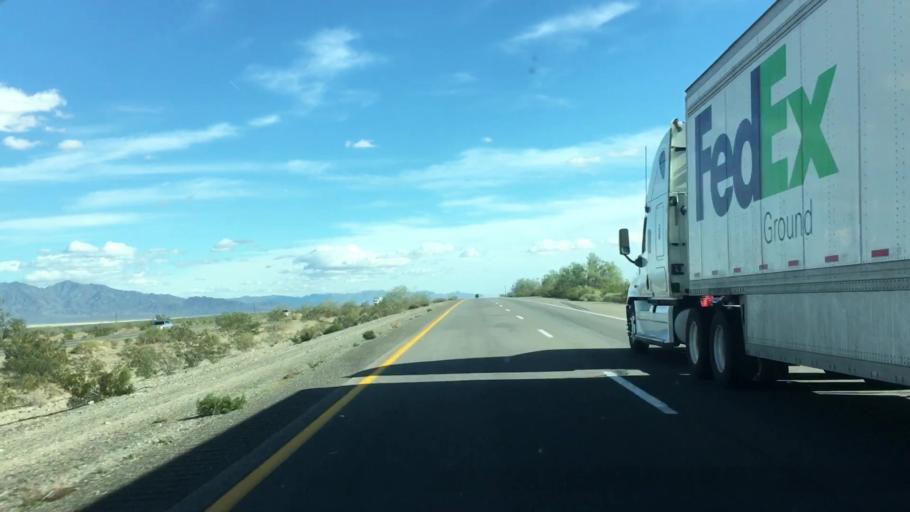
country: US
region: California
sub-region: Imperial County
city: Niland
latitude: 33.7056
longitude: -115.3401
